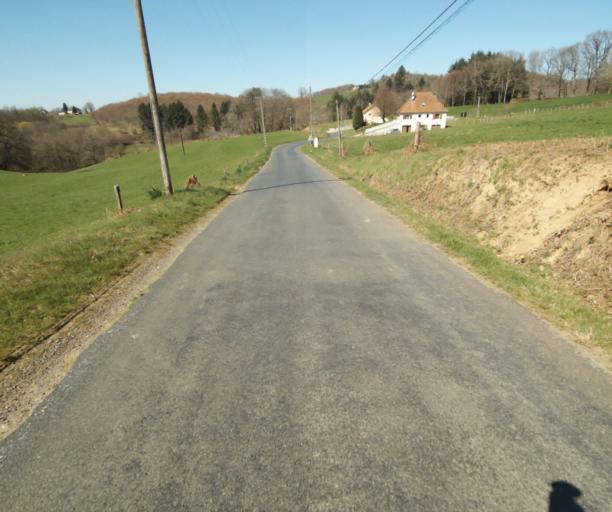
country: FR
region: Limousin
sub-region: Departement de la Correze
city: Saint-Clement
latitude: 45.3383
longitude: 1.7038
